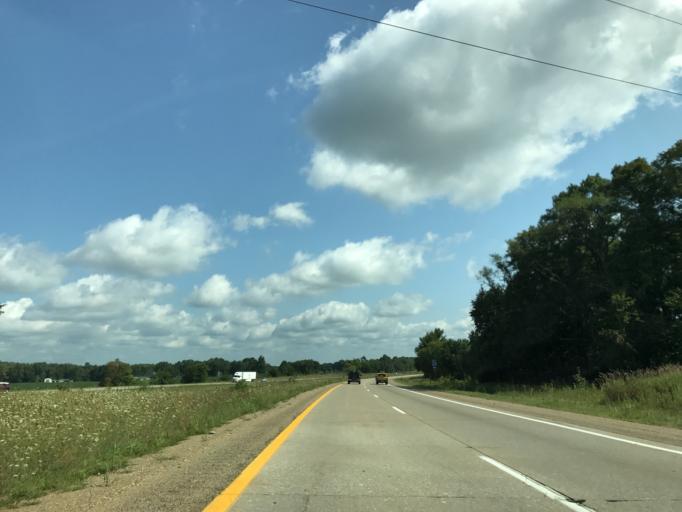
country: US
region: Michigan
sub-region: Branch County
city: Coldwater
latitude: 41.9053
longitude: -84.9888
